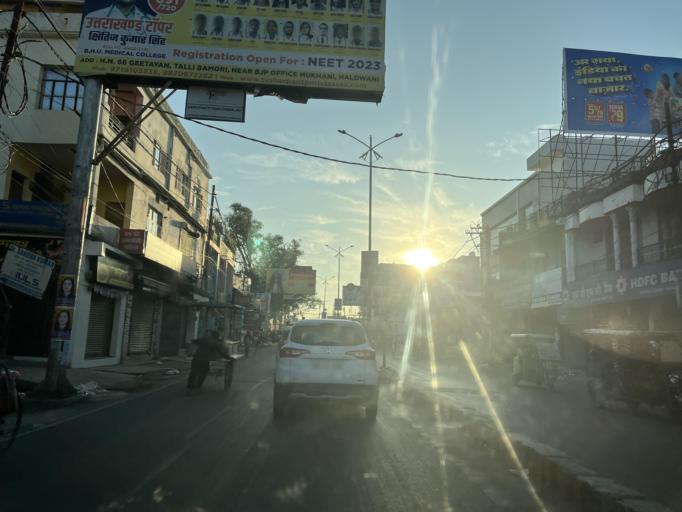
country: IN
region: Uttarakhand
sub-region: Naini Tal
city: Haldwani
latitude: 29.2182
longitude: 79.5175
